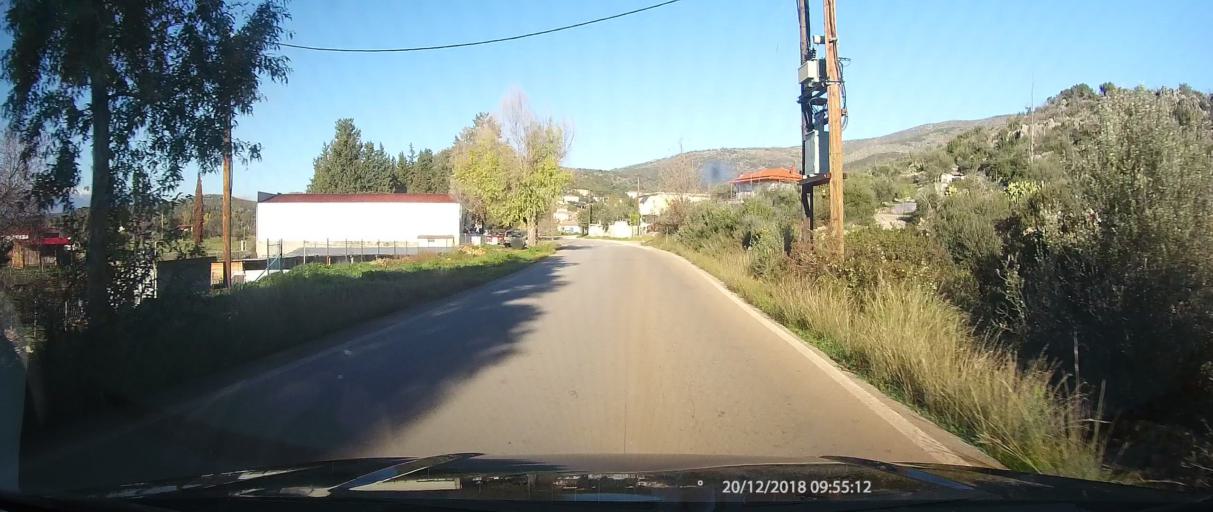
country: GR
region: Peloponnese
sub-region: Nomos Lakonias
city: Yerakion
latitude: 37.0232
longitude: 22.6255
